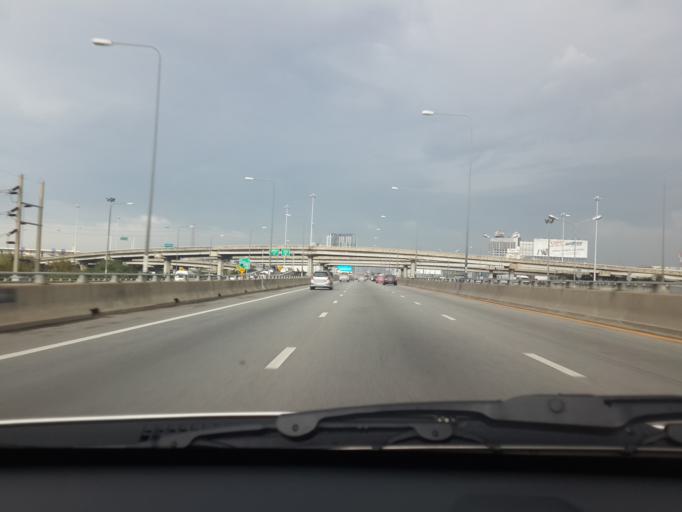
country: TH
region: Bangkok
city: Watthana
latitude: 13.7522
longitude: 100.5918
